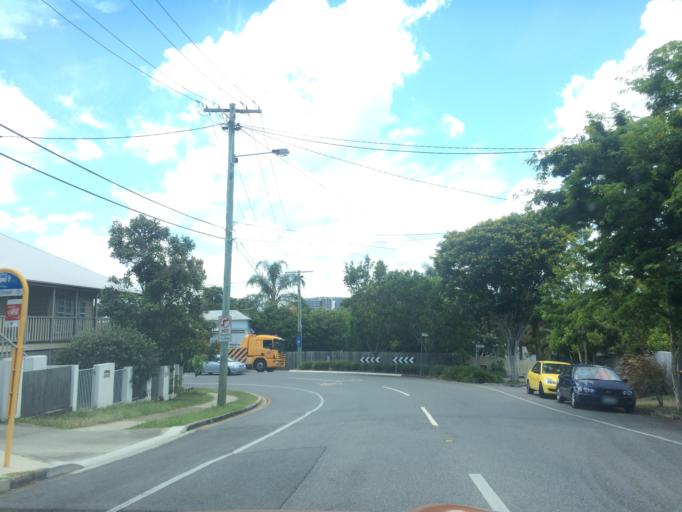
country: AU
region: Queensland
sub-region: Brisbane
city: Toowong
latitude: -27.4867
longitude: 153.0047
